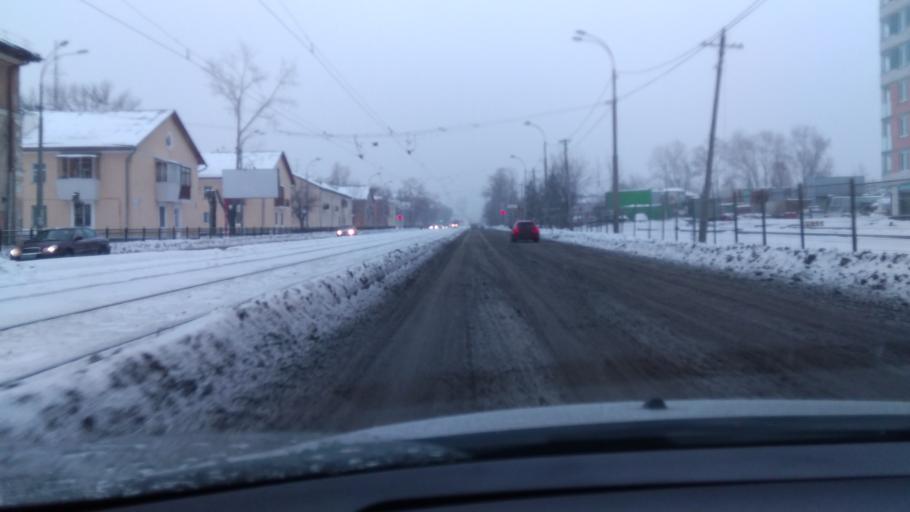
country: RU
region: Sverdlovsk
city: Yekaterinburg
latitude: 56.9016
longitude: 60.5829
